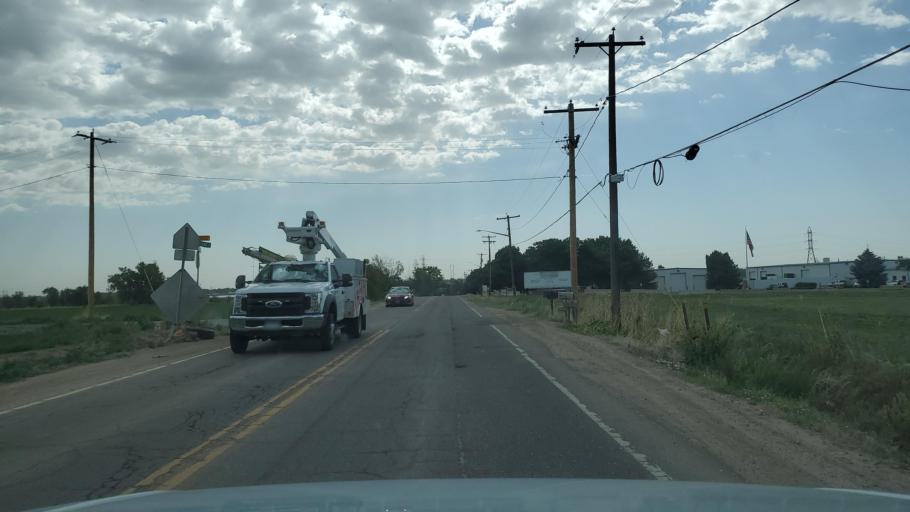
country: US
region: Colorado
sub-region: Adams County
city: Welby
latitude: 39.8381
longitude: -104.9559
